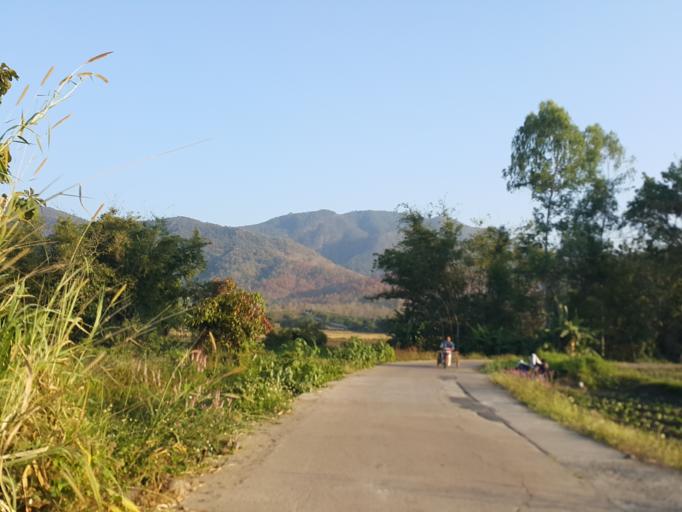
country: TH
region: Chiang Mai
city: Mae On
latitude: 18.7584
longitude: 99.2570
